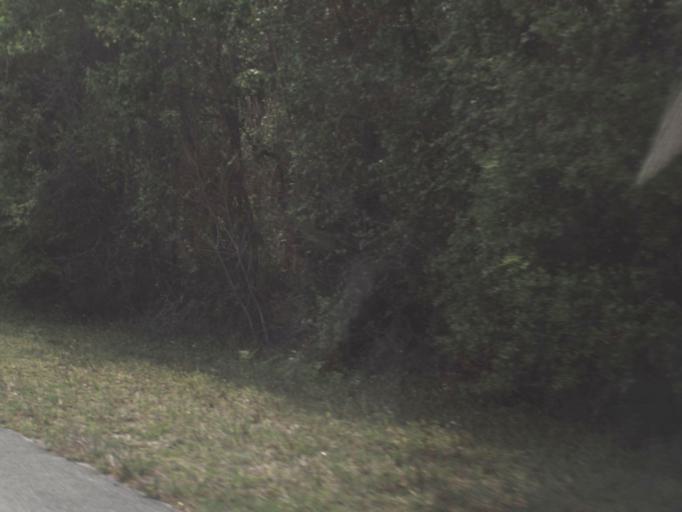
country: US
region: Florida
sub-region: Lake County
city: Astor
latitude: 29.3014
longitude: -81.6726
